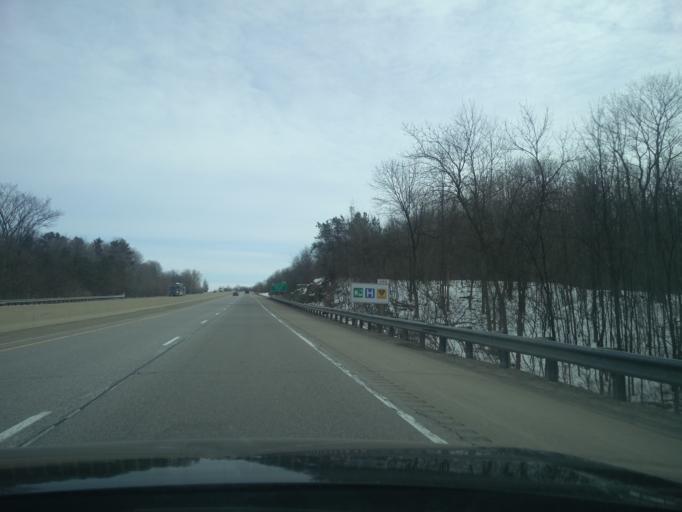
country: CA
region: Ontario
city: Brockville
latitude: 44.5901
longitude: -75.7163
